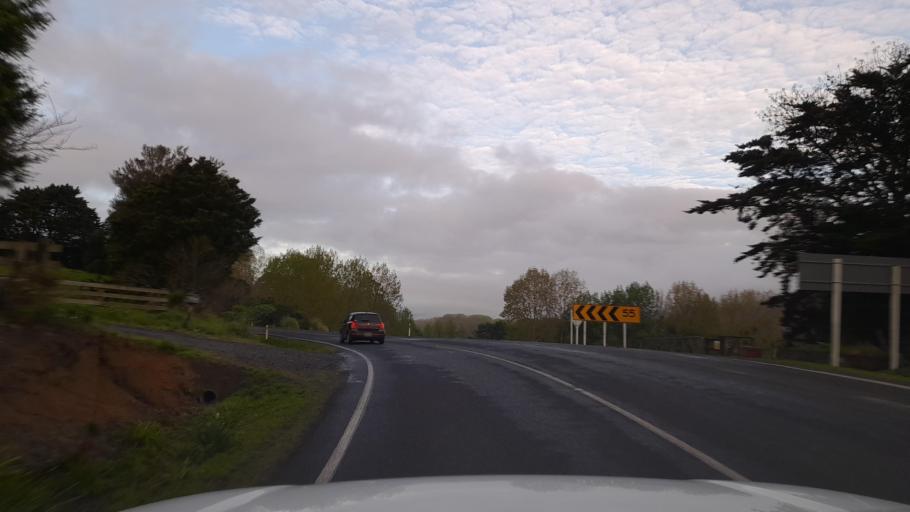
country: NZ
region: Northland
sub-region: Whangarei
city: Maungatapere
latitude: -35.7071
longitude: 173.9824
